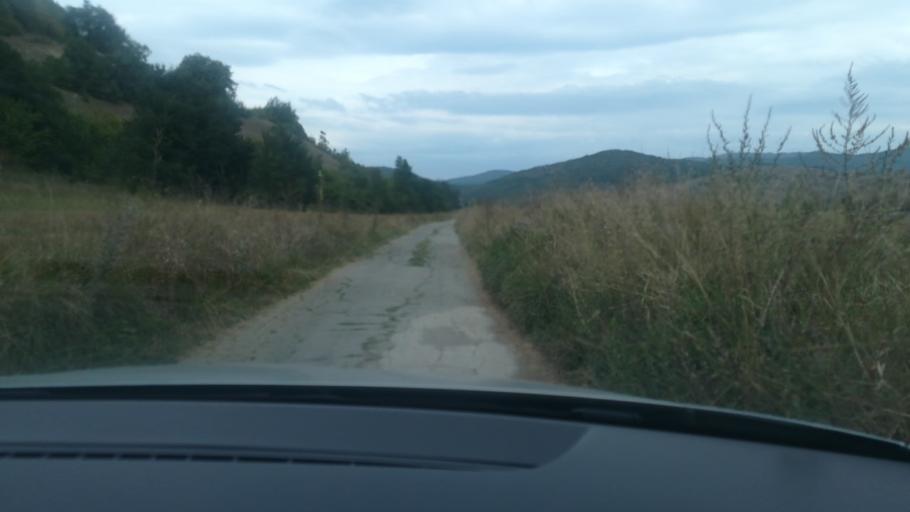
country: MK
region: Debarca
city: Belcista
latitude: 41.2885
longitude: 20.8303
